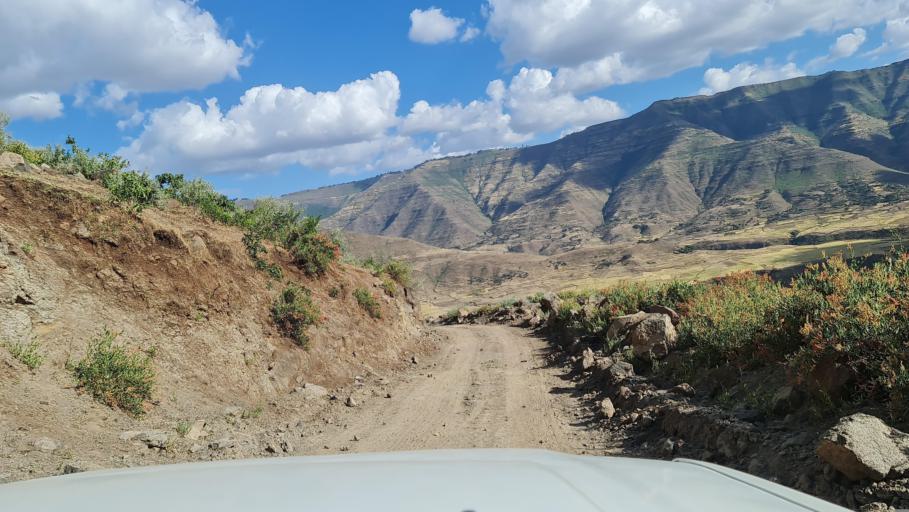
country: ET
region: Amhara
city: Debark'
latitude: 13.1201
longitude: 38.0181
